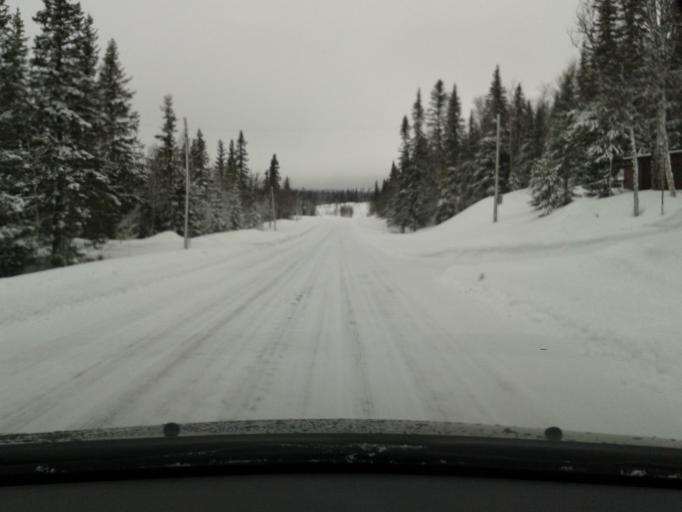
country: SE
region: Vaesterbotten
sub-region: Vilhelmina Kommun
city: Sjoberg
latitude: 65.1827
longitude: 15.9004
